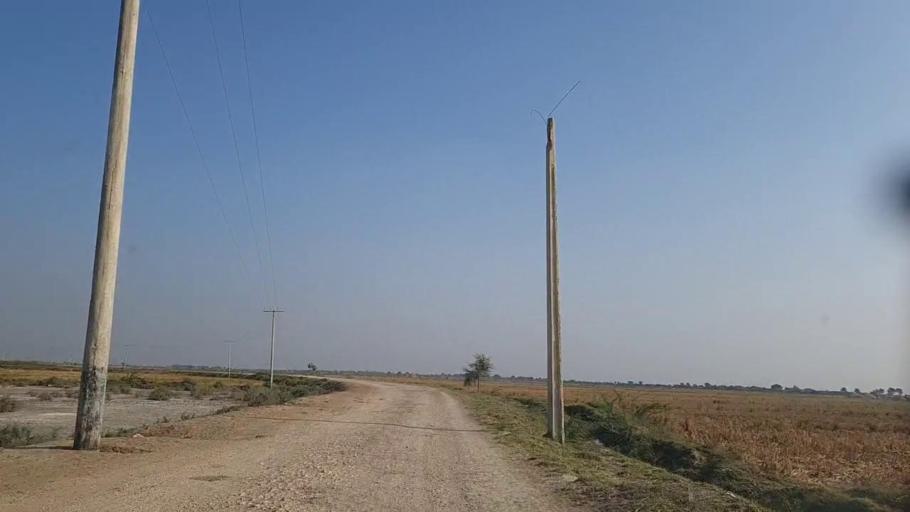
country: PK
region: Sindh
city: Jati
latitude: 24.4619
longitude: 68.2773
